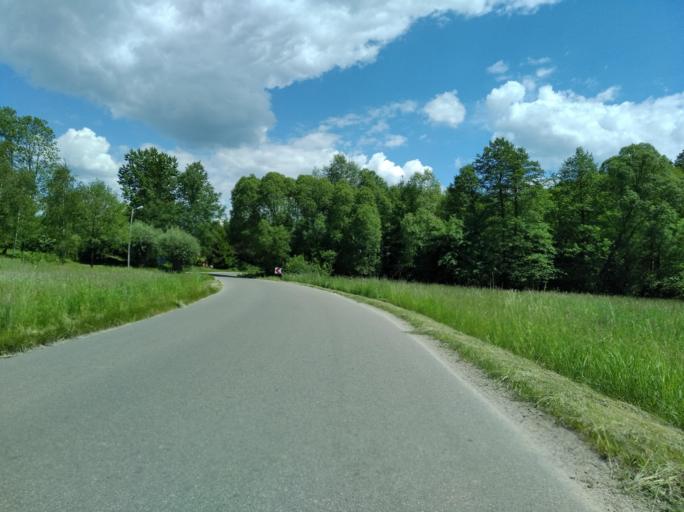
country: PL
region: Subcarpathian Voivodeship
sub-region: Powiat krosnienski
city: Leki
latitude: 49.7854
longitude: 21.6199
